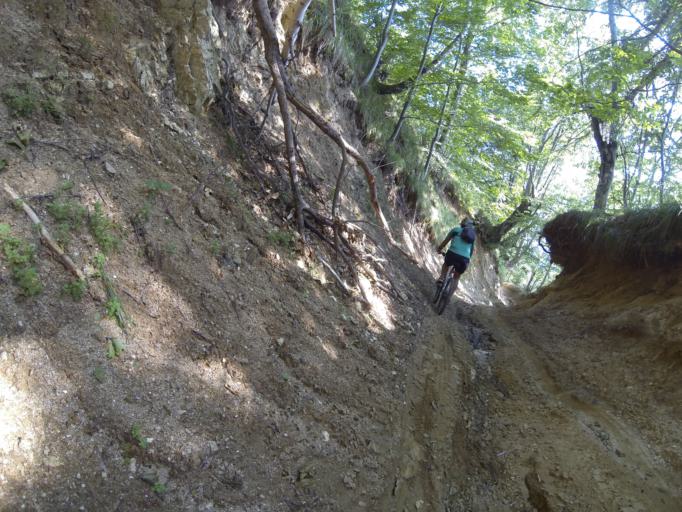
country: RO
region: Valcea
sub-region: Comuna Vaideeni
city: Vaideeni
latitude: 45.2139
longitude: 23.9726
